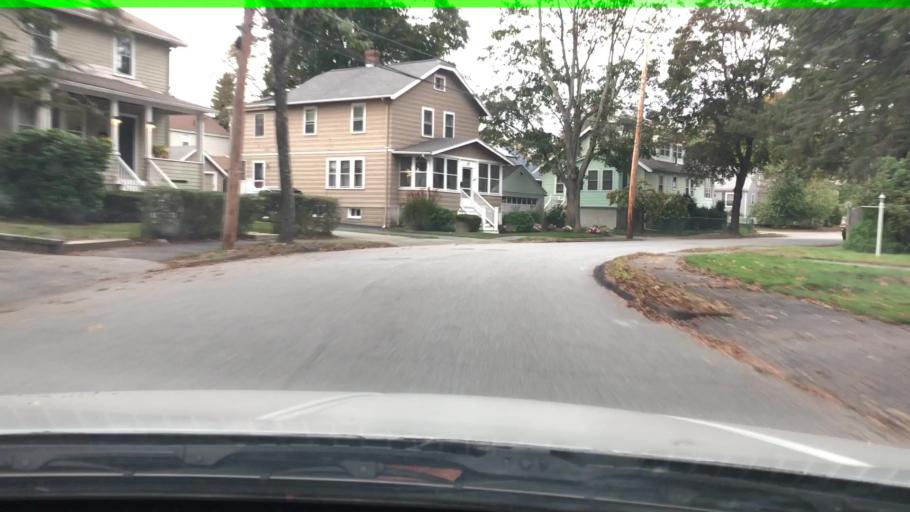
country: US
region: Massachusetts
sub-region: Middlesex County
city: Belmont
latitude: 42.4184
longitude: -71.1908
